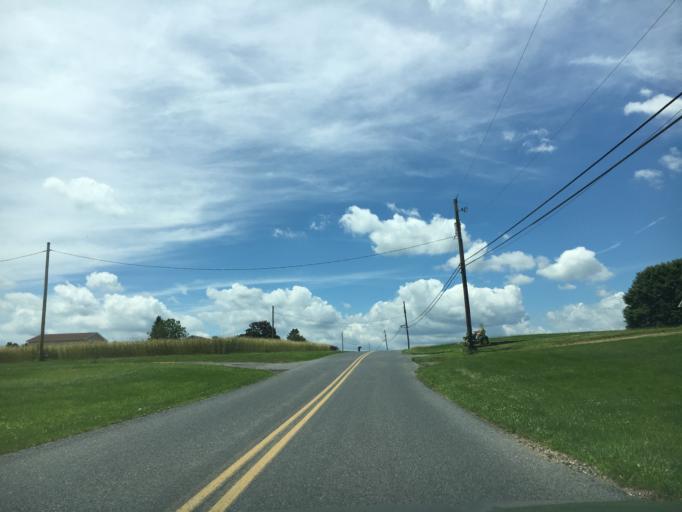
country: US
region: Pennsylvania
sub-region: Lehigh County
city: Laurys Station
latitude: 40.7115
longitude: -75.5565
